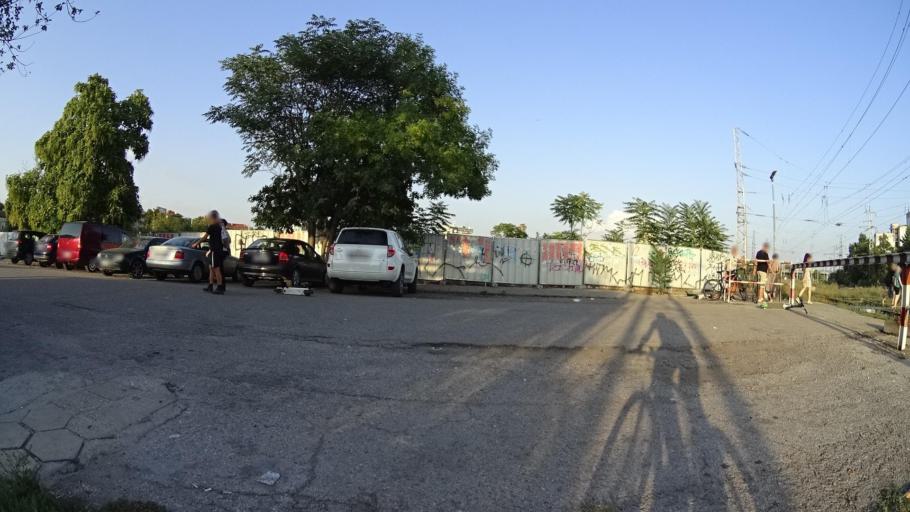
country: BG
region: Plovdiv
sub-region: Obshtina Plovdiv
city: Plovdiv
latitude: 42.1349
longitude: 24.7503
